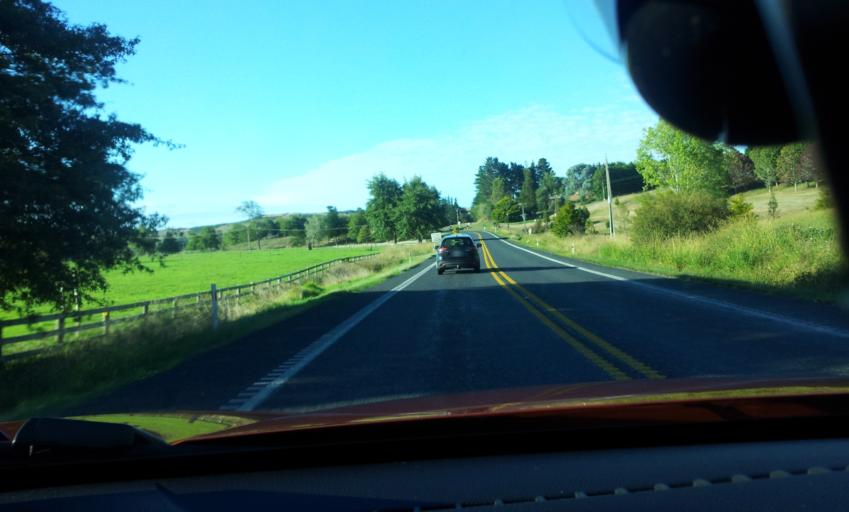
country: NZ
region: Waikato
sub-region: Waikato District
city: Te Kauwhata
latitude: -37.2378
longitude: 175.1712
